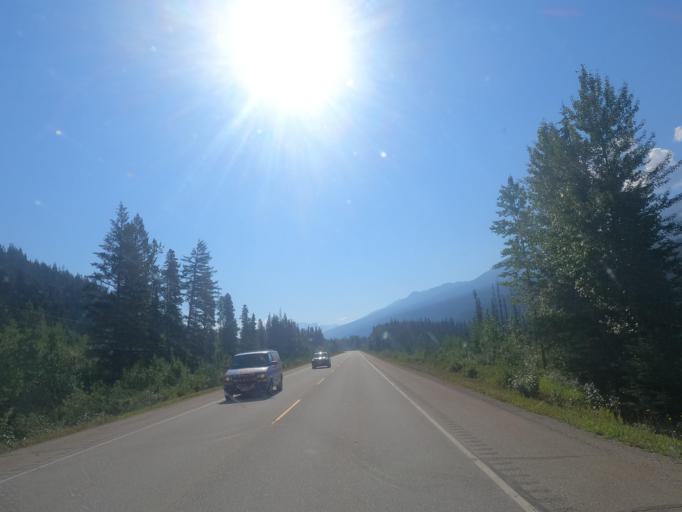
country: CA
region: Alberta
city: Jasper Park Lodge
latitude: 52.9122
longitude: -118.7872
